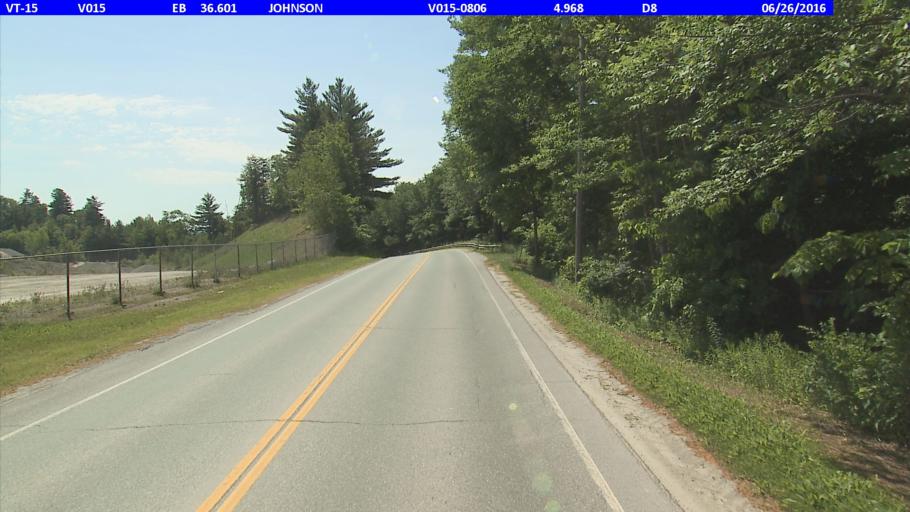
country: US
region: Vermont
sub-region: Lamoille County
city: Johnson
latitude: 44.6247
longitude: -72.6767
